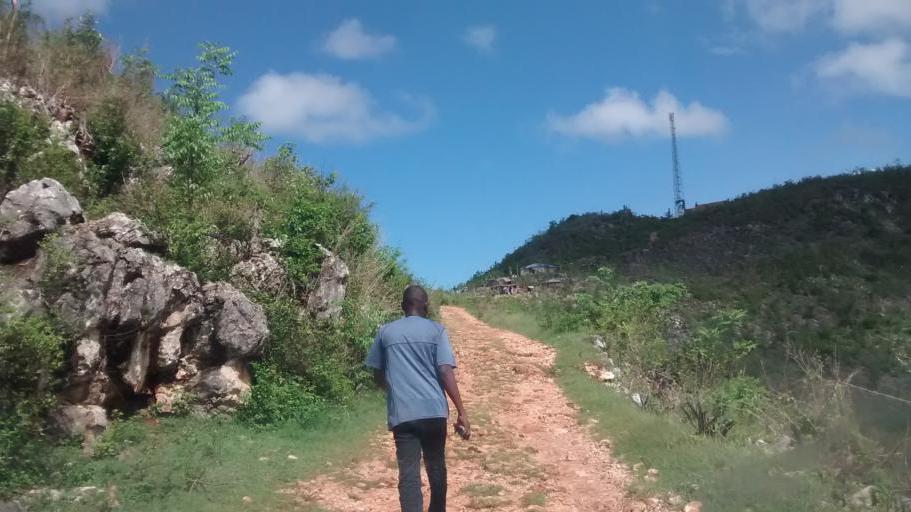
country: HT
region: Grandans
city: Corail
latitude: 18.5398
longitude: -73.9196
